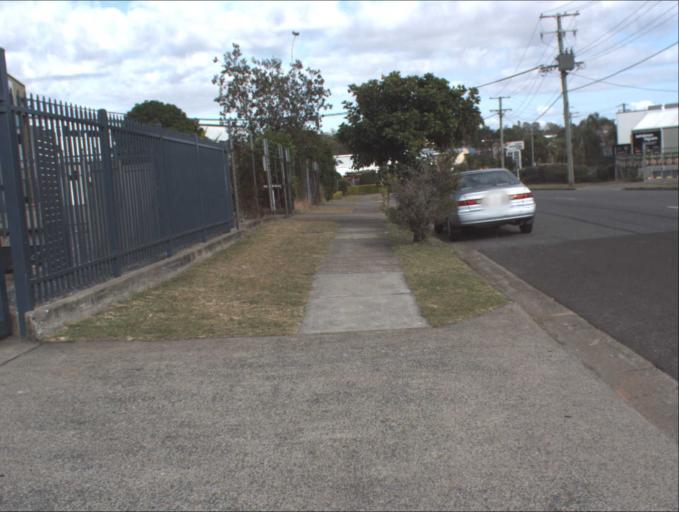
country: AU
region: Queensland
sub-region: Logan
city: Springwood
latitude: -27.6160
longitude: 153.1185
